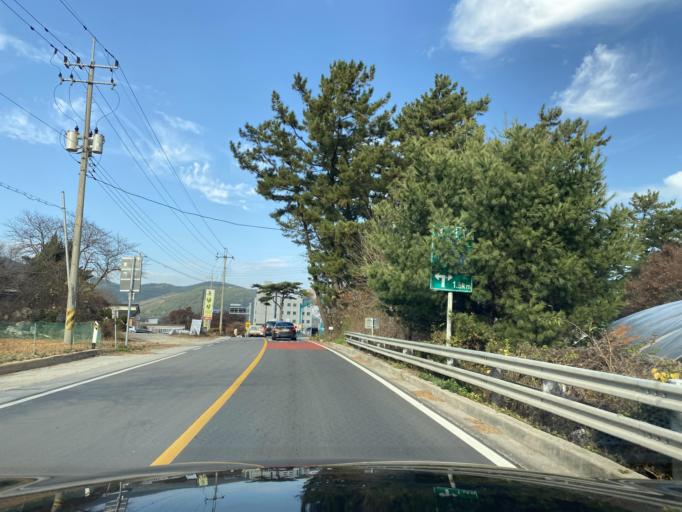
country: KR
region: Chungcheongnam-do
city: Hongsung
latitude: 36.6727
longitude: 126.6424
